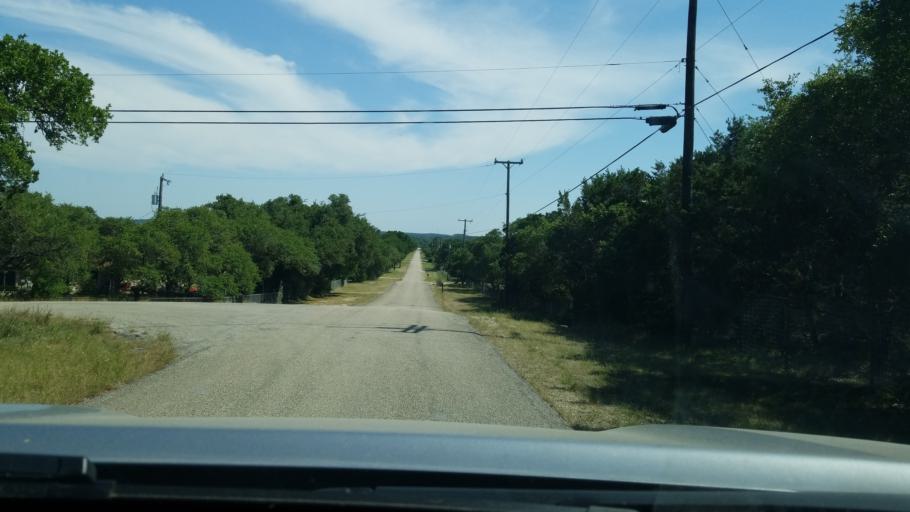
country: US
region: Texas
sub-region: Bexar County
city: Timberwood Park
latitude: 29.7591
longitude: -98.5179
